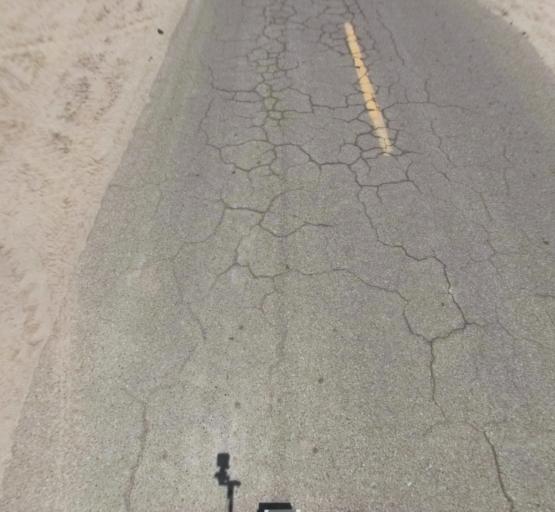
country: US
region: California
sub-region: Fresno County
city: Kerman
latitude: 36.8246
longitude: -120.1509
